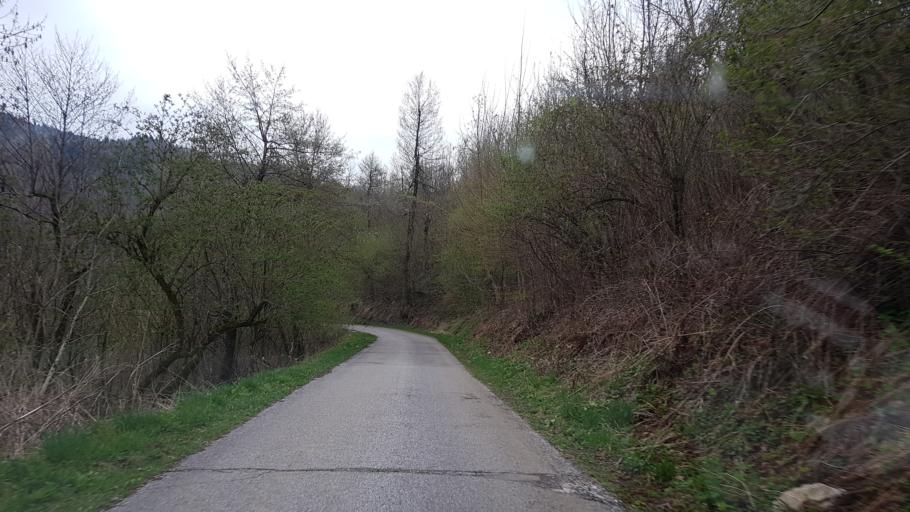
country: IT
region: Friuli Venezia Giulia
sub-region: Provincia di Udine
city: Faedis
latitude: 46.1836
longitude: 13.3930
